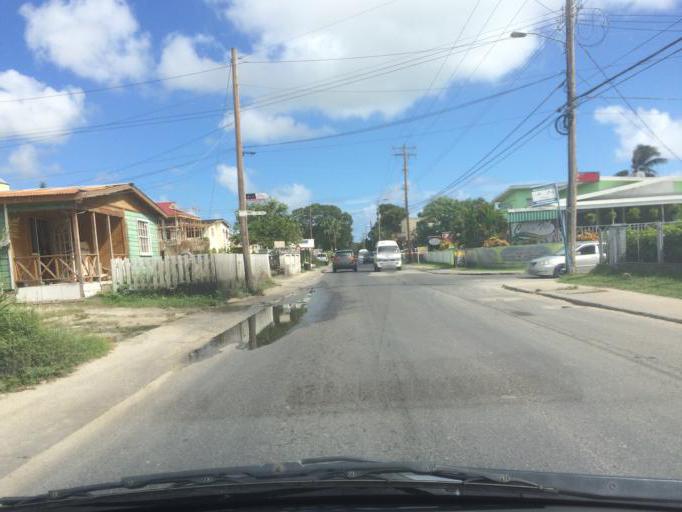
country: BB
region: Christ Church
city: Oistins
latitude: 13.0692
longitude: -59.5608
